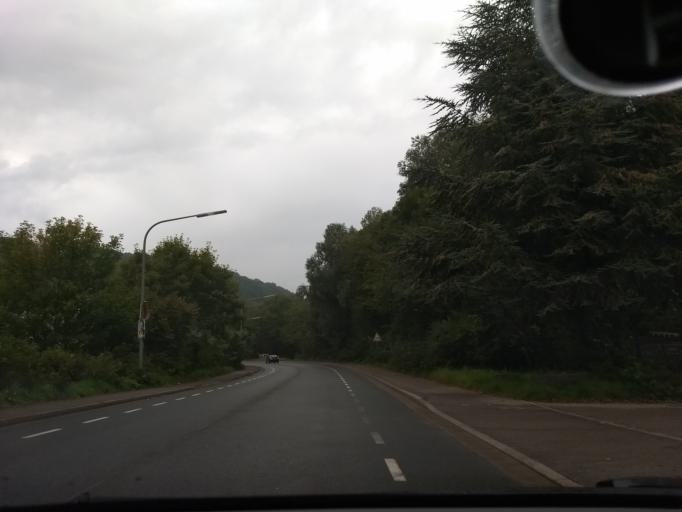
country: DE
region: North Rhine-Westphalia
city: Wickede
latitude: 51.4570
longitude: 7.9726
